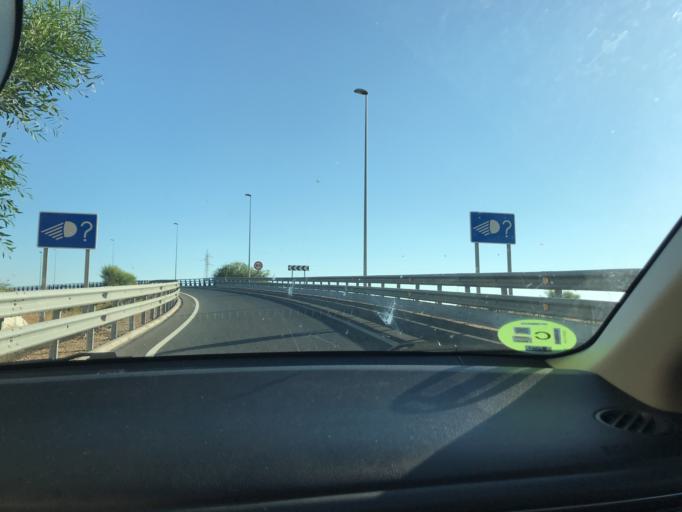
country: ES
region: Andalusia
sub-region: Provincia de Sevilla
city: Alcala de Guadaira
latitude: 37.4329
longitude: -5.8454
